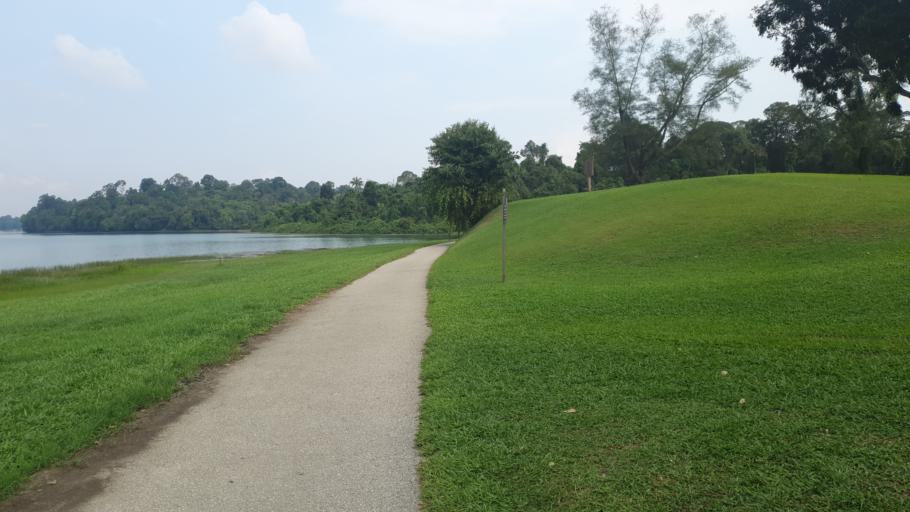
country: SG
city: Singapore
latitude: 1.3443
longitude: 103.8147
